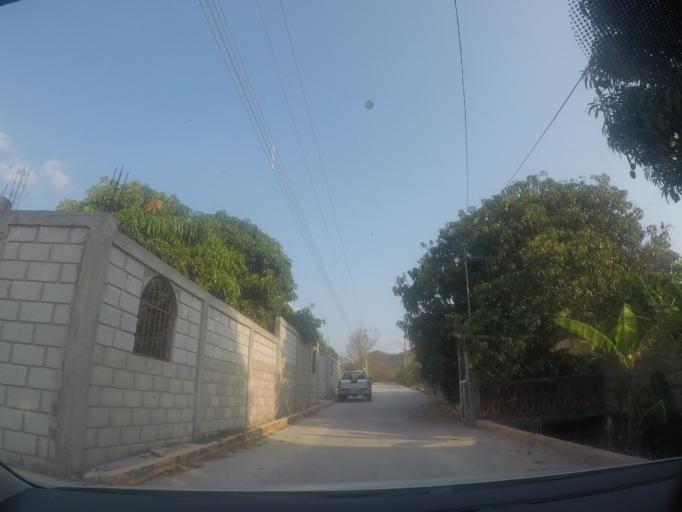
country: MX
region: Oaxaca
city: San Jeronimo Ixtepec
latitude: 16.5816
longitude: -95.1984
